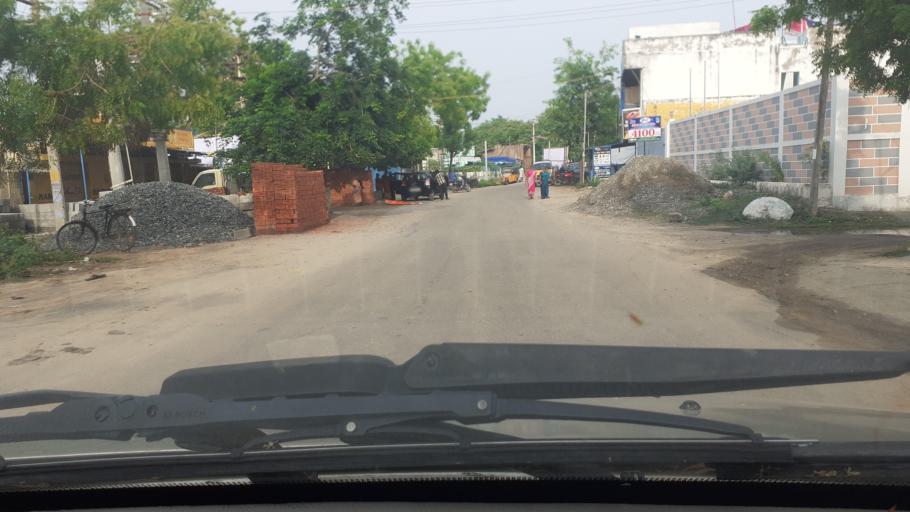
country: IN
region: Tamil Nadu
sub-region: Thoothukkudi
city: Korampallam
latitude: 8.7915
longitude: 78.1128
